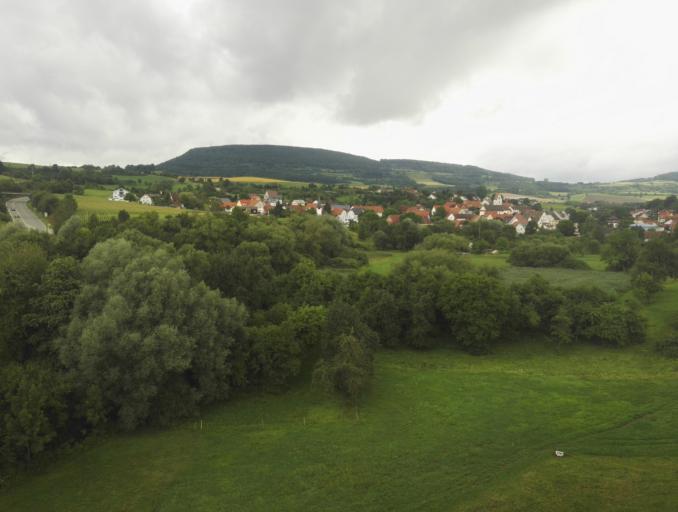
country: DE
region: Baden-Wuerttemberg
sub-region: Freiburg Region
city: Blumberg
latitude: 47.8023
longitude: 8.5272
